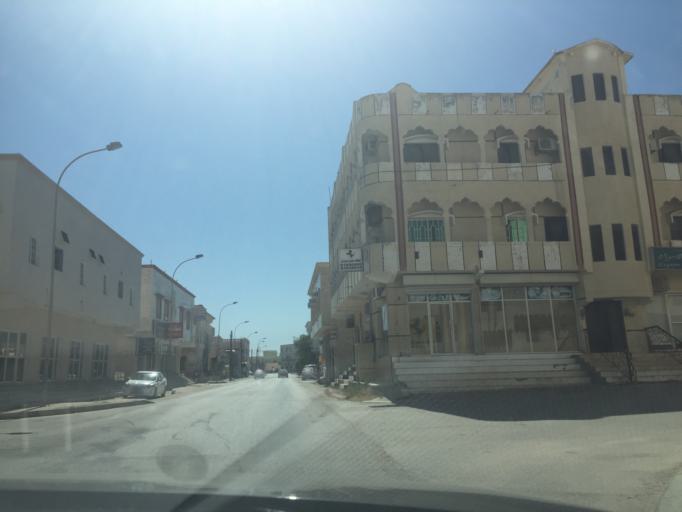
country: OM
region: Zufar
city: Salalah
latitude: 17.0239
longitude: 54.1564
